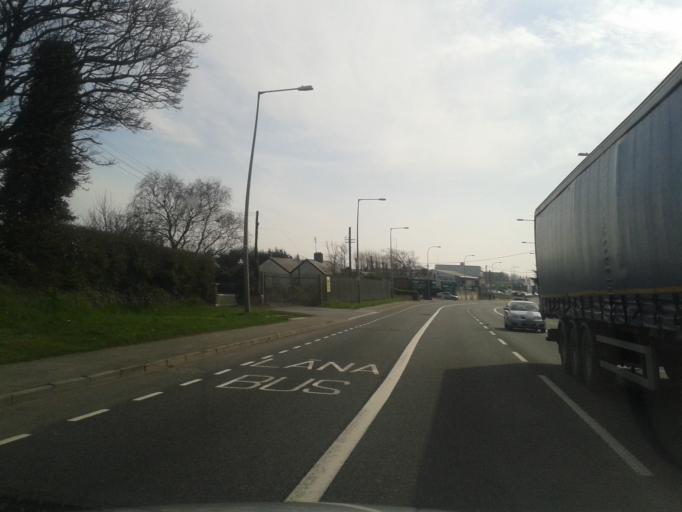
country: IE
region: Leinster
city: Beaumont
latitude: 53.4151
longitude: -6.2392
